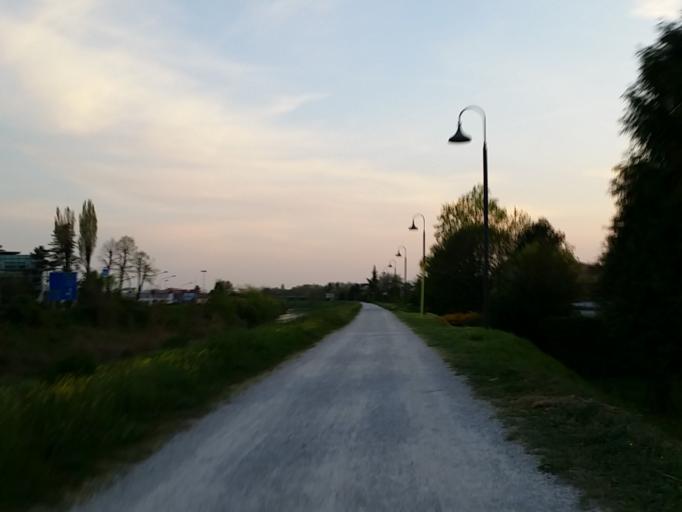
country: IT
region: Veneto
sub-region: Provincia di Padova
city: Mandriola-Sant'Agostino
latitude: 45.3793
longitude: 11.8530
